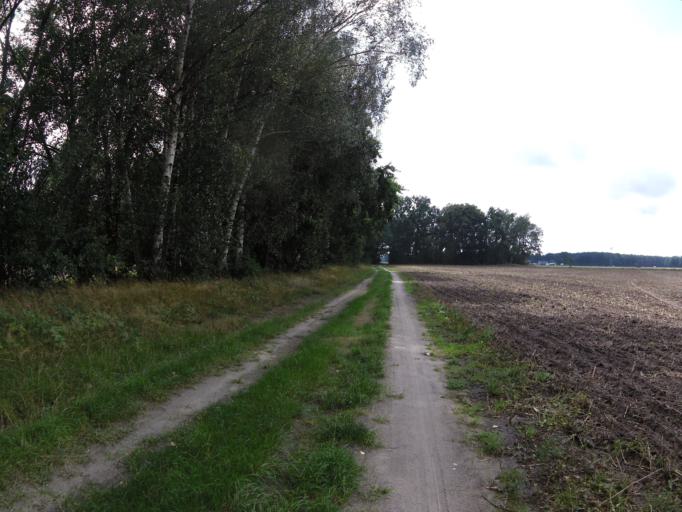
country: DE
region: Brandenburg
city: Storkow
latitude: 52.2734
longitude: 13.9332
